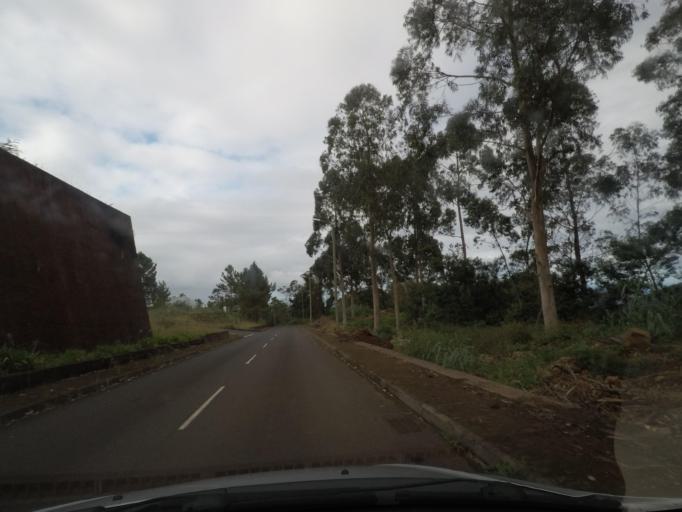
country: PT
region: Madeira
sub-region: Santana
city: Santana
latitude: 32.7865
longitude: -16.8786
